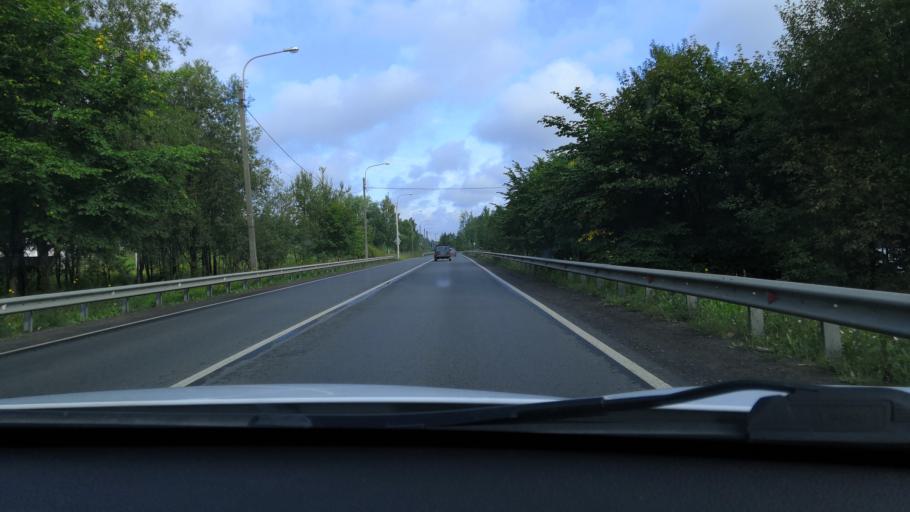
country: RU
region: St.-Petersburg
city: Tyarlevo
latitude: 59.7027
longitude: 30.4397
